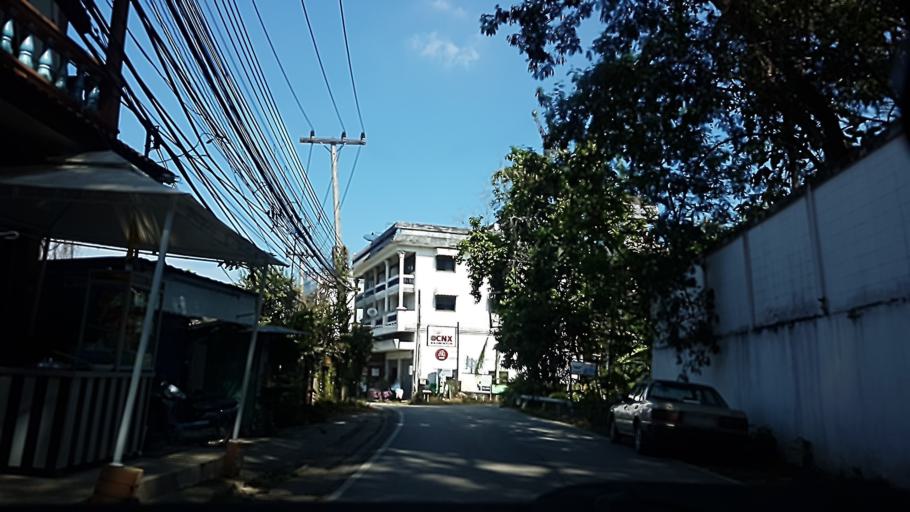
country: TH
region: Chiang Mai
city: Chiang Mai
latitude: 18.8423
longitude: 98.9749
